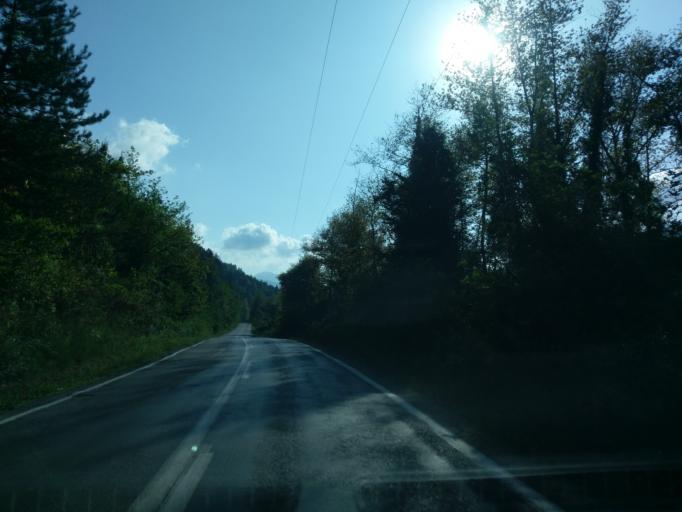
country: TR
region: Sinop
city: Yenikonak
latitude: 41.8856
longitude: 34.5663
